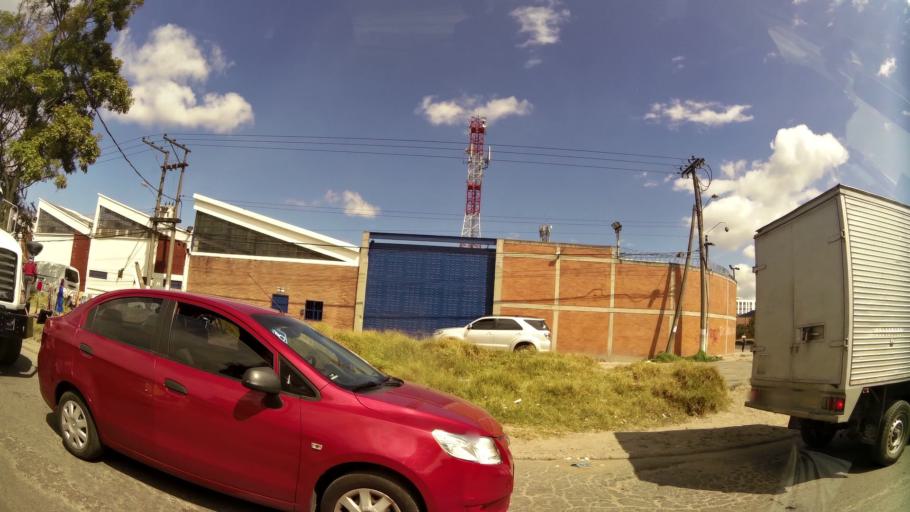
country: CO
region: Bogota D.C.
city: Bogota
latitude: 4.6328
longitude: -74.1120
